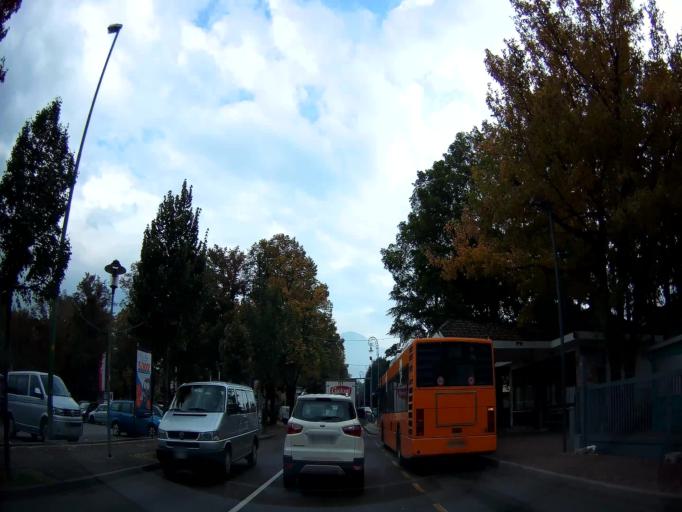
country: IT
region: Trentino-Alto Adige
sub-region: Bolzano
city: Merano
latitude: 46.6740
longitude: 11.1491
